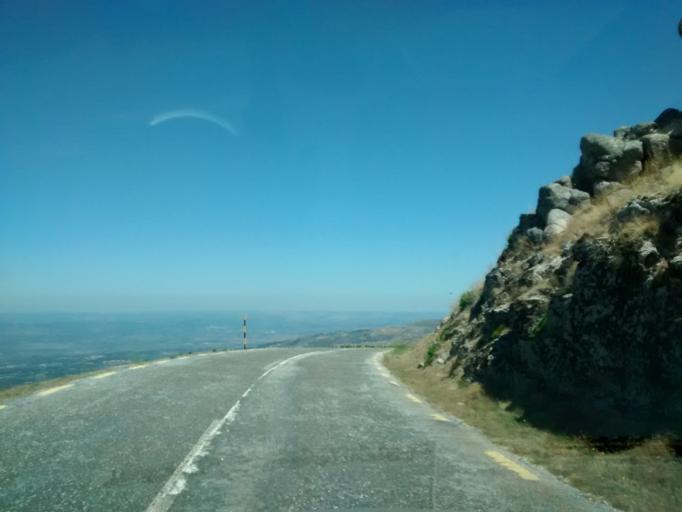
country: PT
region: Guarda
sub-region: Seia
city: Seia
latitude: 40.4227
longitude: -7.6254
